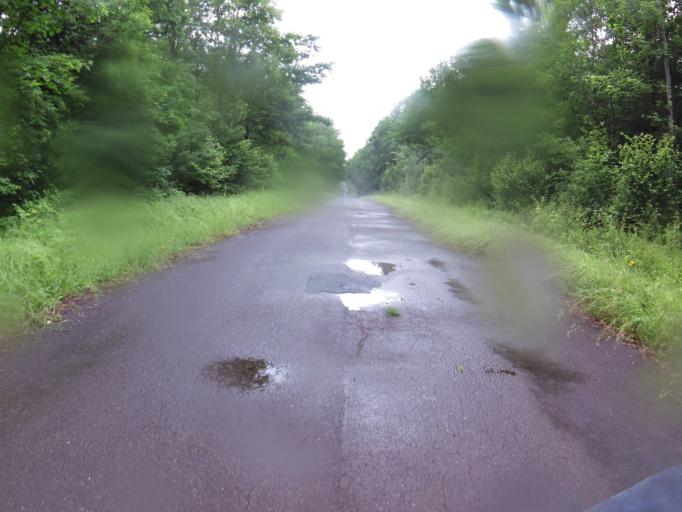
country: FR
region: Champagne-Ardenne
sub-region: Departement de la Haute-Marne
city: Chancenay
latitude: 48.7431
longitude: 4.9822
